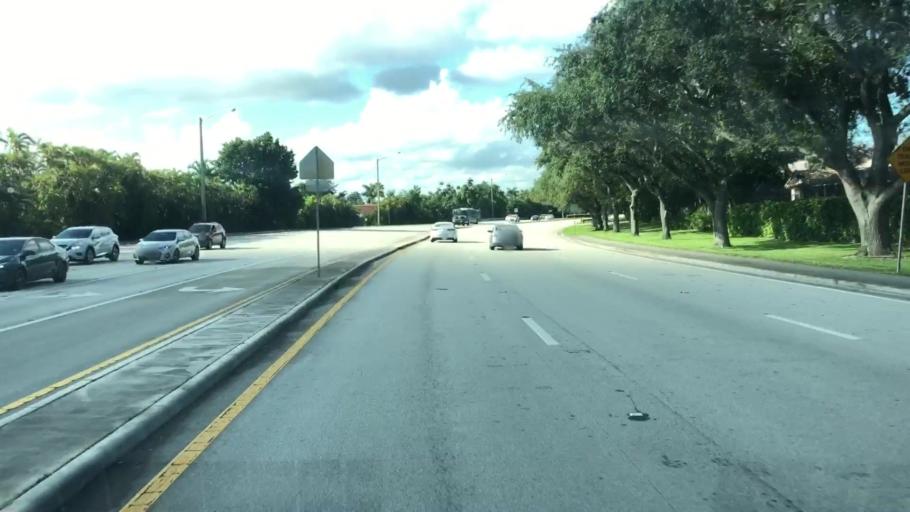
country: US
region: Florida
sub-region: Broward County
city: Coral Springs
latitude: 26.2402
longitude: -80.2690
